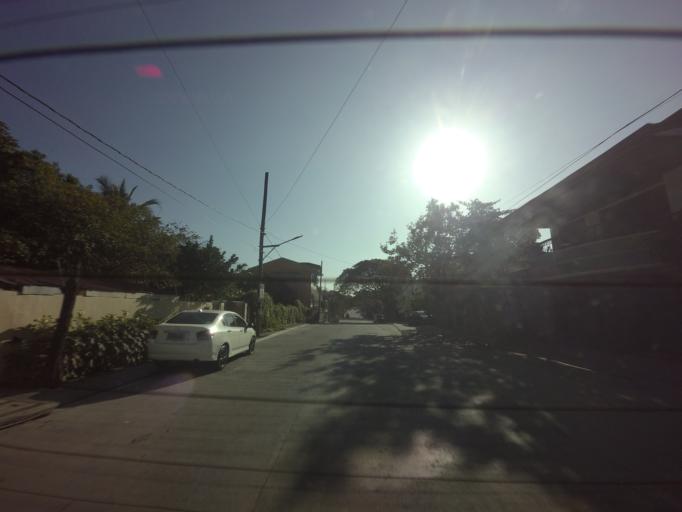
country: PH
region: Metro Manila
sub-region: Makati City
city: Makati City
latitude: 14.5304
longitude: 121.0374
